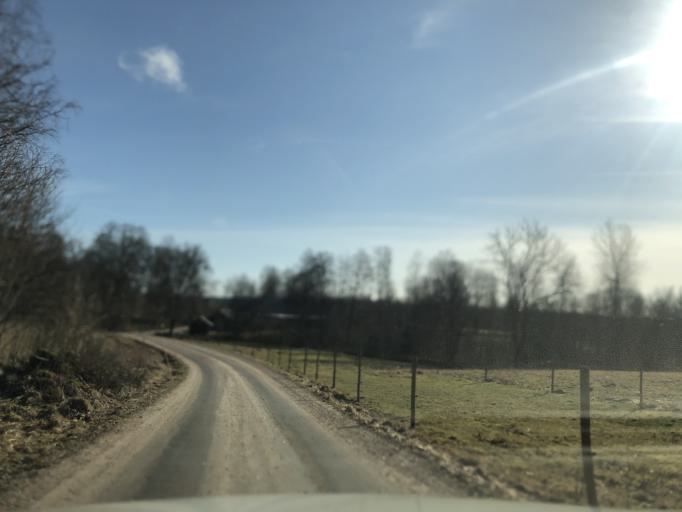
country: SE
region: Vaestra Goetaland
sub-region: Ulricehamns Kommun
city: Ulricehamn
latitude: 57.8070
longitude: 13.3897
